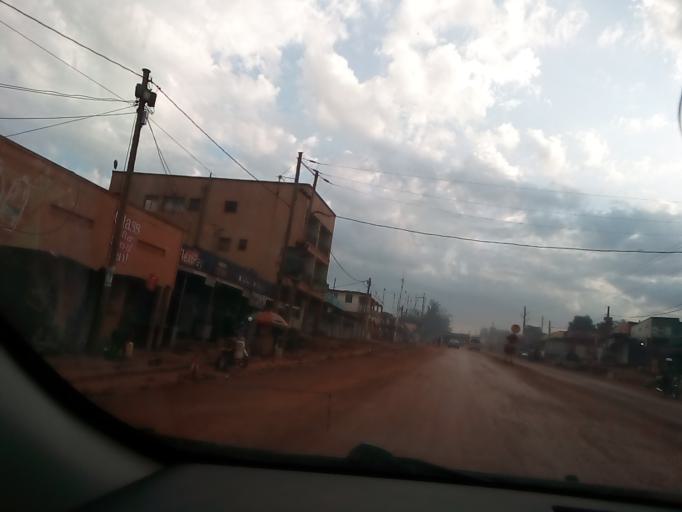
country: UG
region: Central Region
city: Masaka
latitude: -0.3152
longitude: 31.7607
